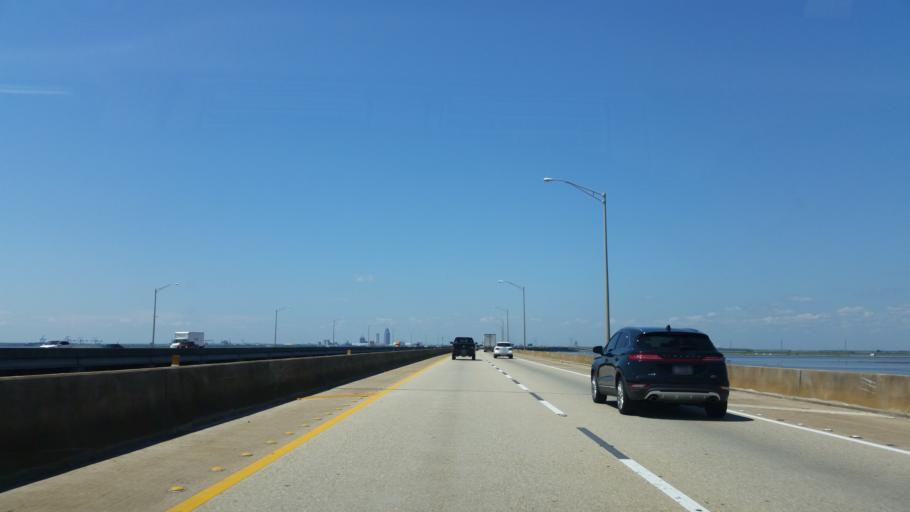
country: US
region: Alabama
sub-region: Baldwin County
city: Spanish Fort
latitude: 30.6684
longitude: -87.9712
